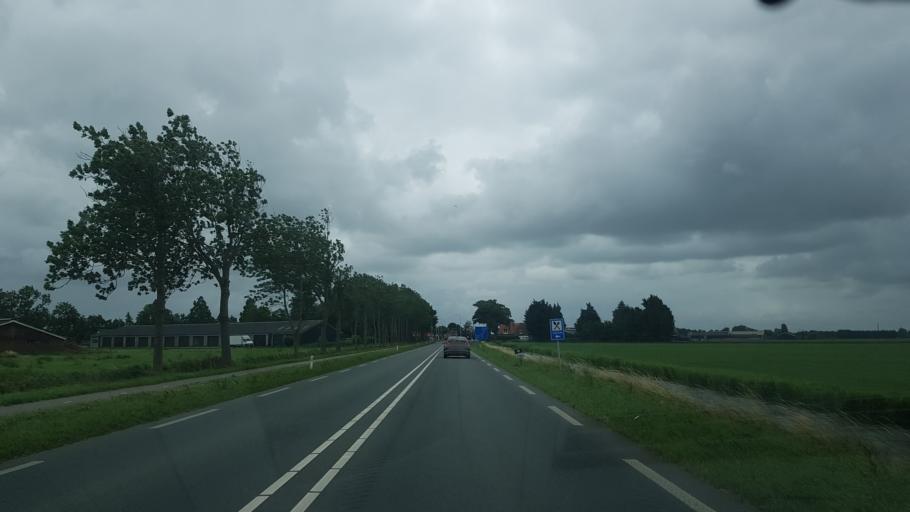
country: NL
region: North Holland
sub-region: Gemeente Hoorn
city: Hoorn
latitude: 52.6597
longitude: 5.1455
